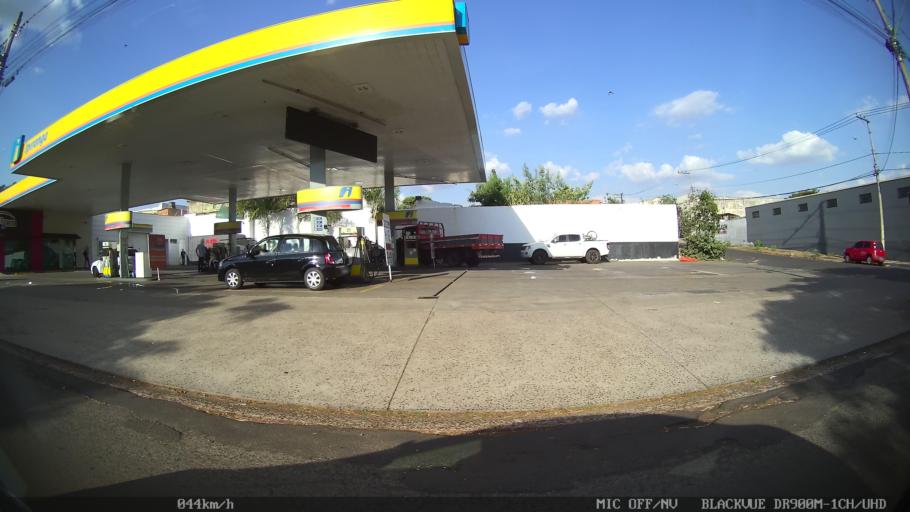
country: BR
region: Sao Paulo
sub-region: Ribeirao Preto
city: Ribeirao Preto
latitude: -21.1409
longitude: -47.7987
